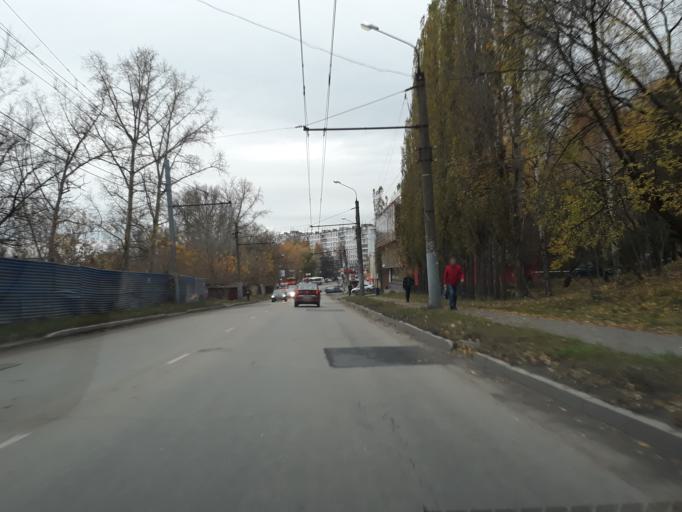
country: RU
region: Nizjnij Novgorod
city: Afonino
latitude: 56.2842
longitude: 44.0541
